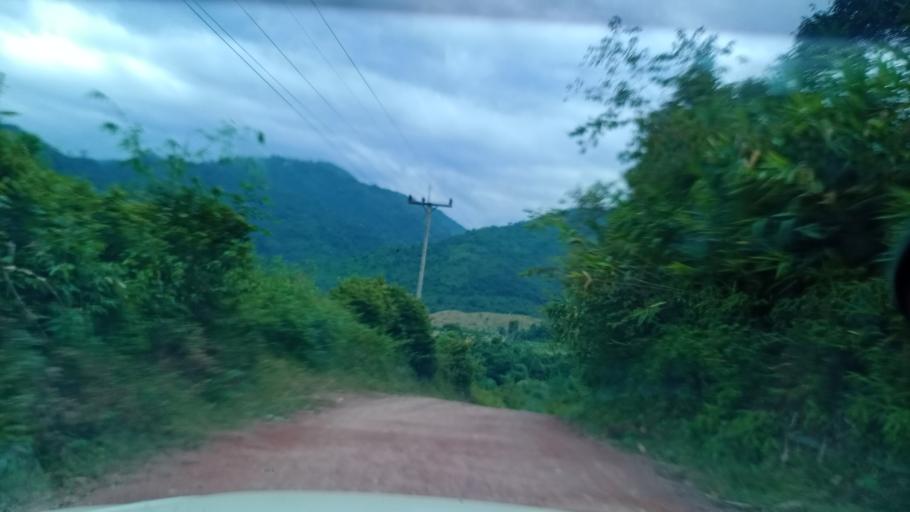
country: TH
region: Changwat Bueng Kan
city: Pak Khat
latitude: 18.7198
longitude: 103.2270
